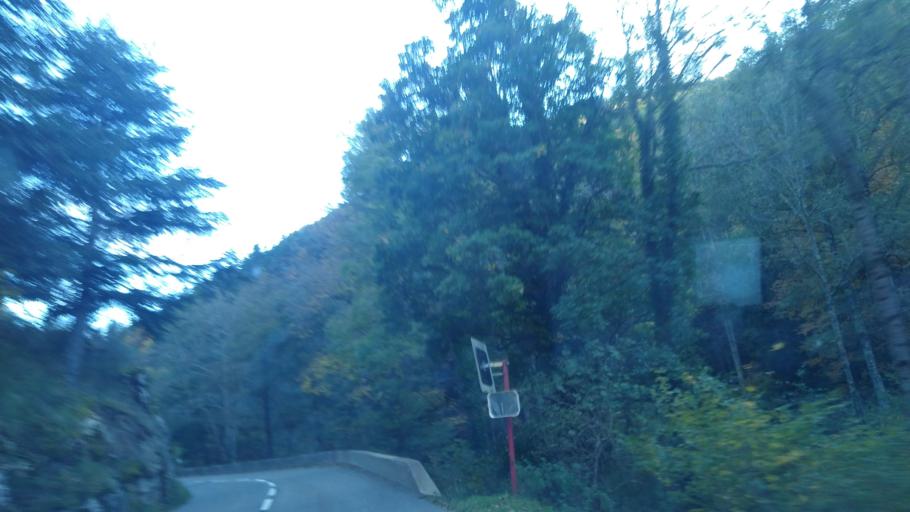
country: FR
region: Languedoc-Roussillon
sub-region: Departement de l'Aude
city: Quillan
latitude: 42.7328
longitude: 2.1000
